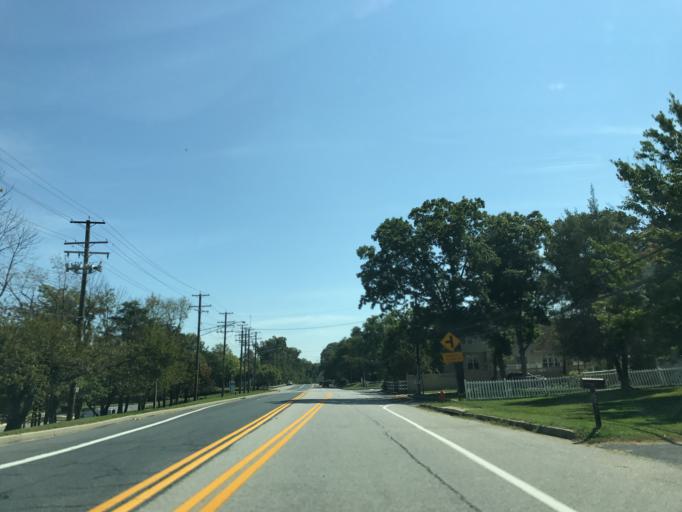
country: US
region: Maryland
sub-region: Howard County
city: Hanover
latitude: 39.1844
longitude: -76.7560
